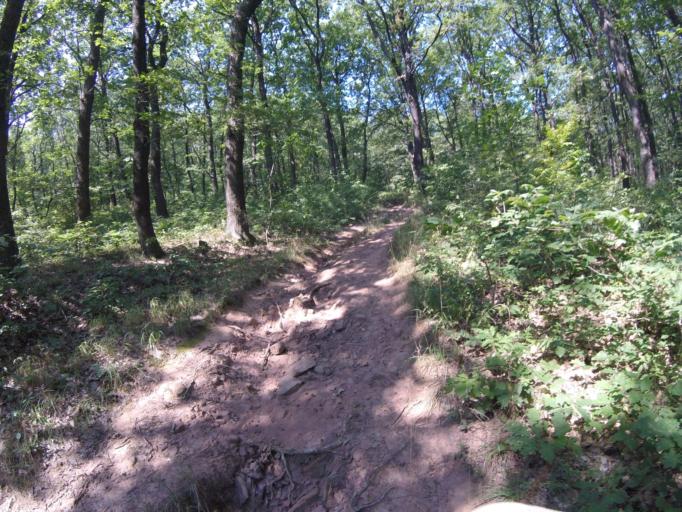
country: HU
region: Baranya
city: Pellerd
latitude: 46.0913
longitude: 18.1675
